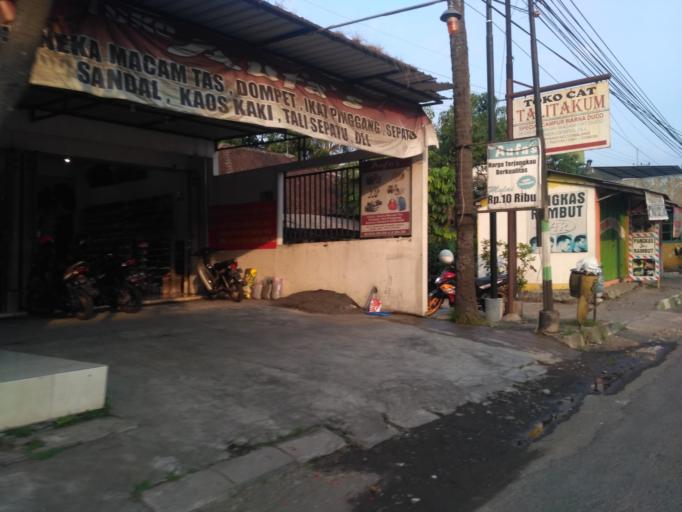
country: ID
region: East Java
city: Kepuh
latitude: -8.0034
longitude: 112.6178
